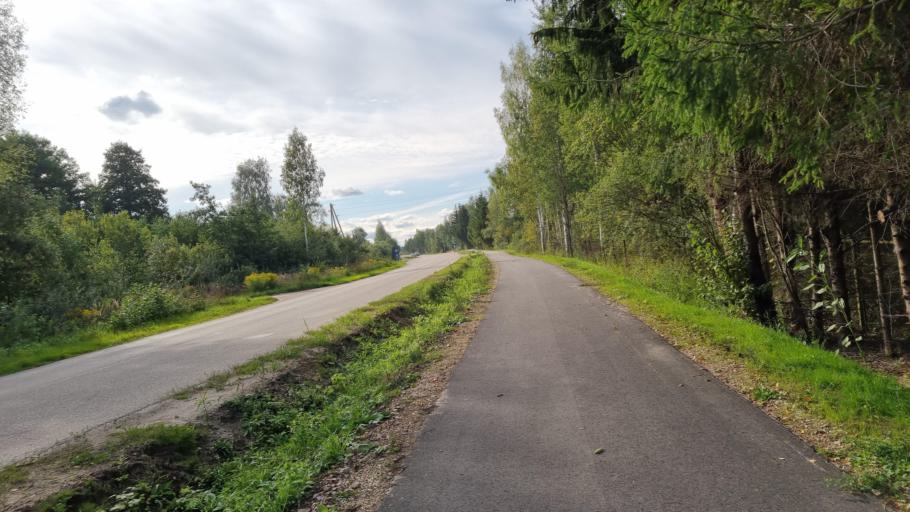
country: LV
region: Lecava
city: Iecava
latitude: 56.6991
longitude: 24.0780
